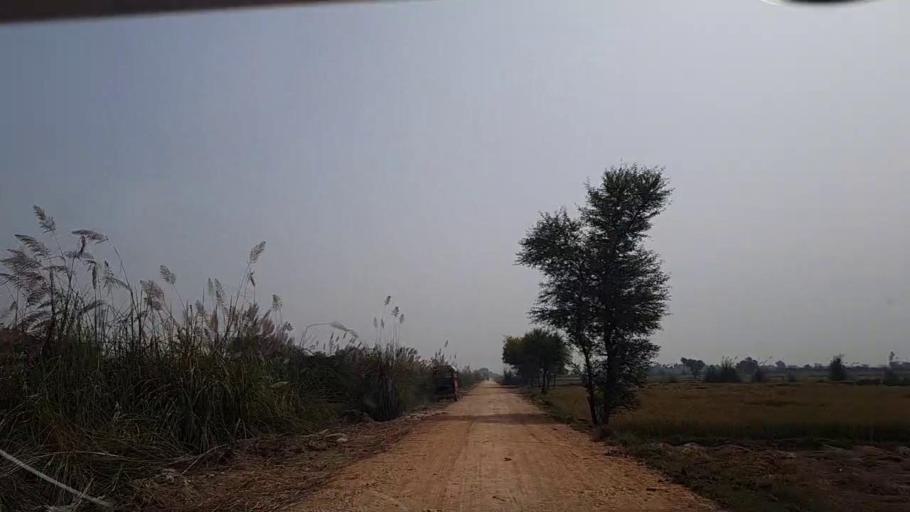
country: PK
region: Sindh
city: Garhi Yasin
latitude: 27.9283
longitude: 68.5616
